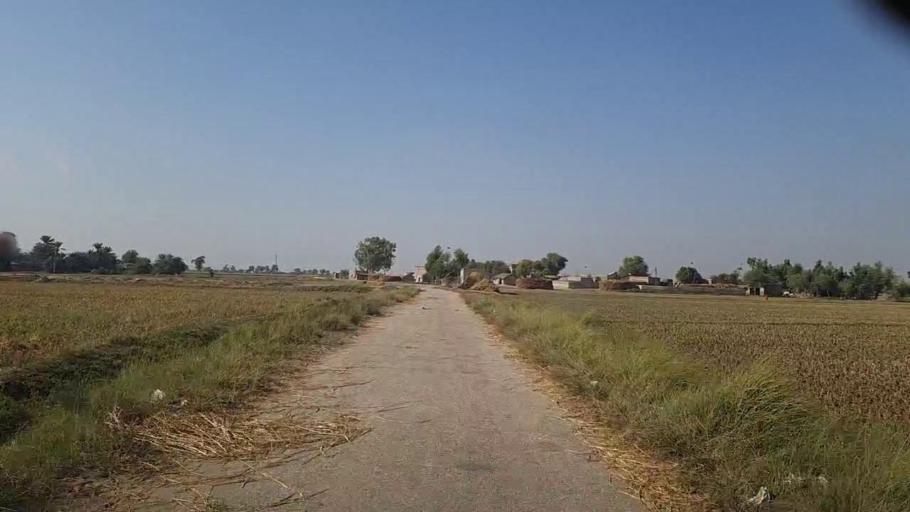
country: PK
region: Sindh
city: Tangwani
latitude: 28.2658
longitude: 68.9306
